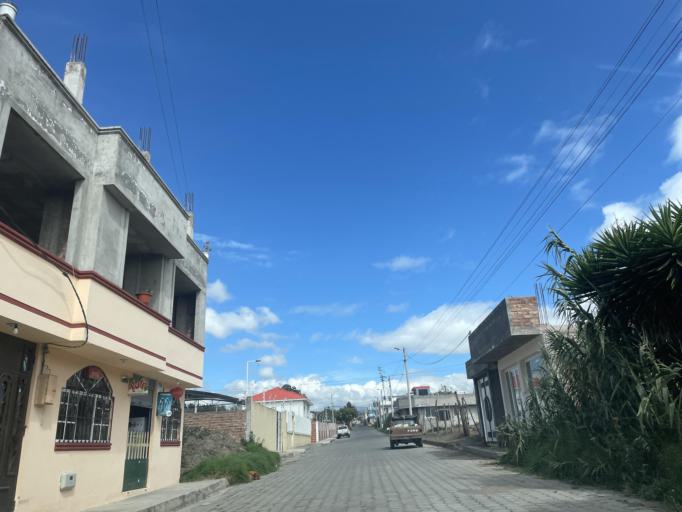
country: EC
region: Chimborazo
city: Guano
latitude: -1.6051
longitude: -78.6406
